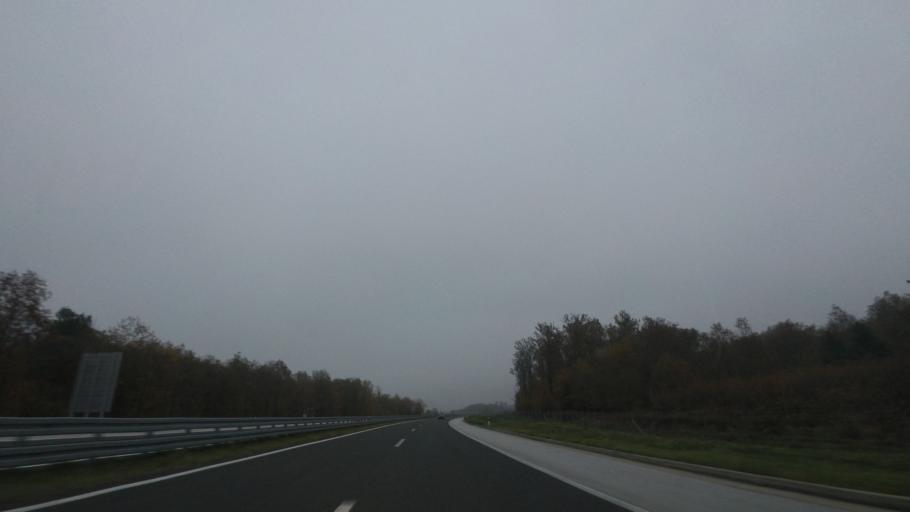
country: HR
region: Zagrebacka
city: Turopolje
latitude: 45.6129
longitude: 16.1154
